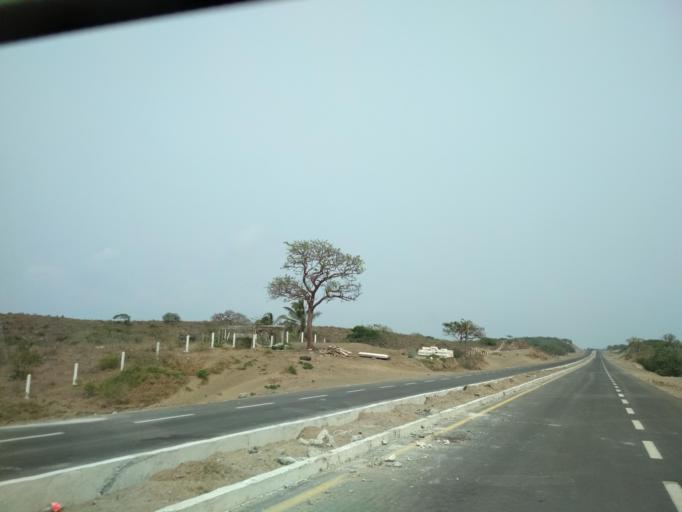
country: MX
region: Veracruz
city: Anton Lizardo
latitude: 19.0450
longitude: -95.9966
